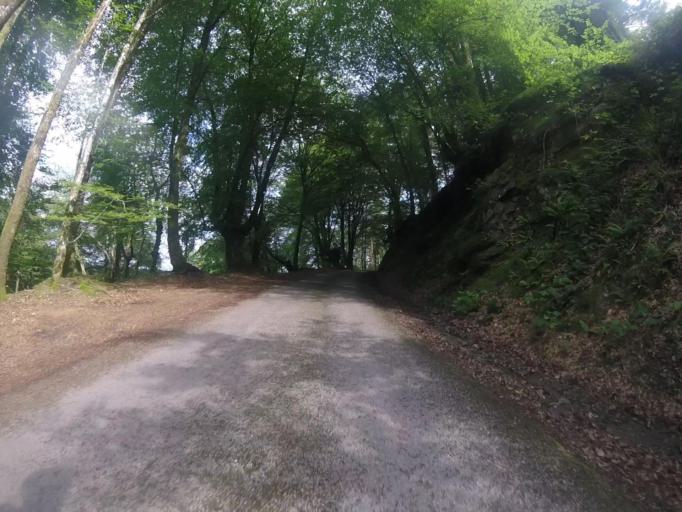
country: ES
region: Navarre
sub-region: Provincia de Navarra
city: Goizueta
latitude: 43.2324
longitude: -1.8059
